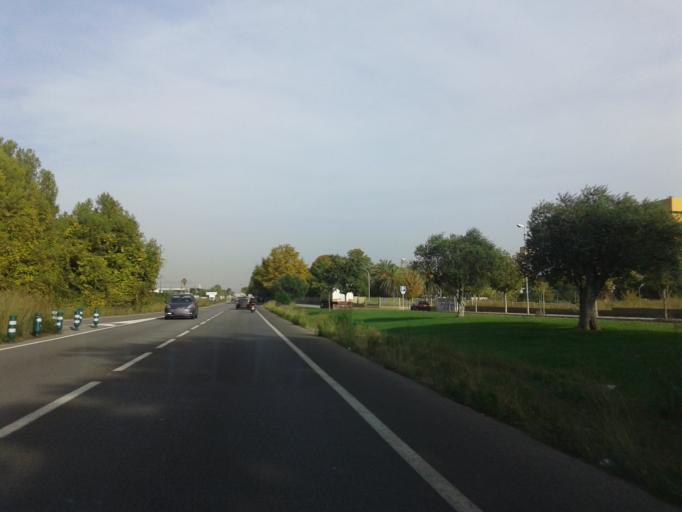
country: ES
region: Catalonia
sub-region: Provincia de Tarragona
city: Cunit
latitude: 41.2021
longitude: 1.6502
